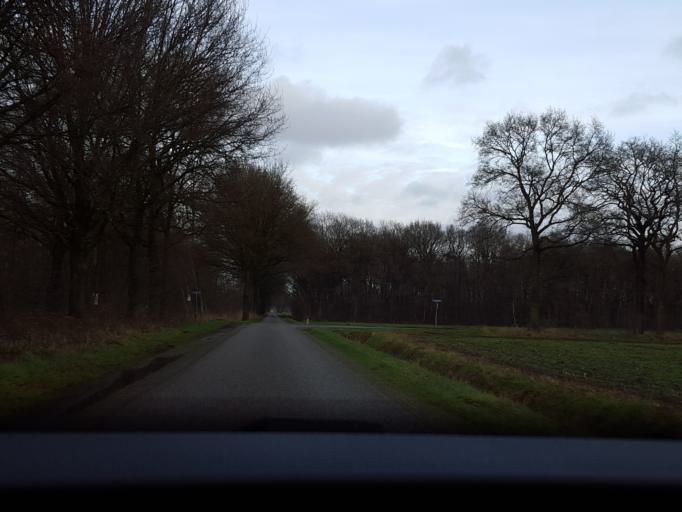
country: NL
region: Gelderland
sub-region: Oost Gelre
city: Lichtenvoorde
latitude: 52.0146
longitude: 6.5579
